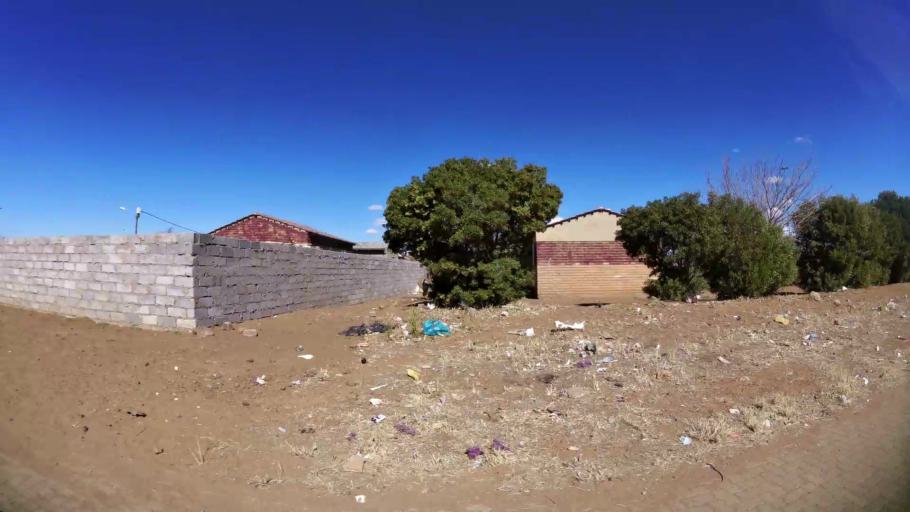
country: ZA
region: North-West
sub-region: Dr Kenneth Kaunda District Municipality
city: Klerksdorp
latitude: -26.8655
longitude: 26.5664
